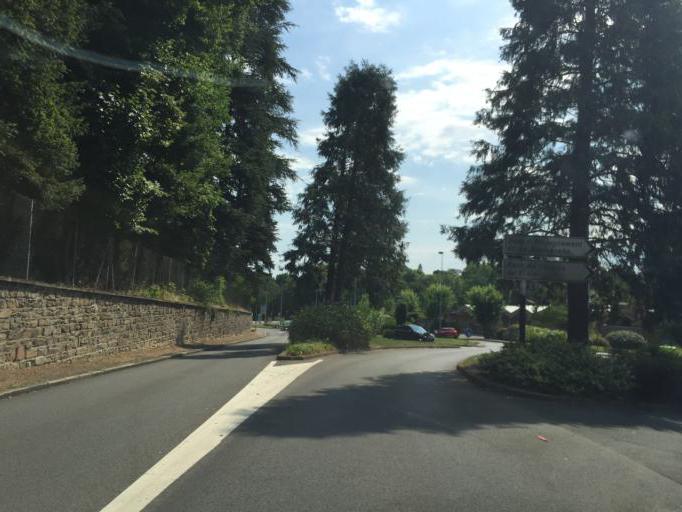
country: FR
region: Rhone-Alpes
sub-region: Departement du Rhone
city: Ecully
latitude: 45.7681
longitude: 4.7695
